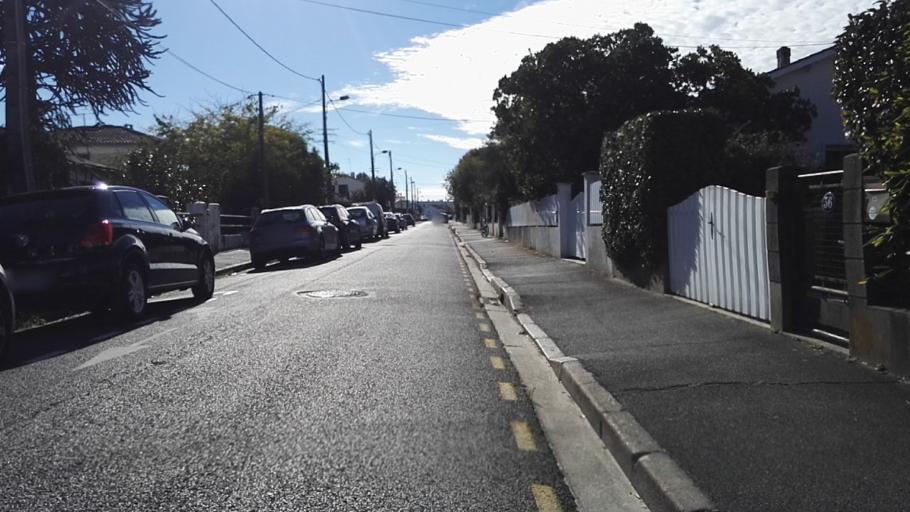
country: FR
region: Aquitaine
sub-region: Departement de la Gironde
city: Eysines
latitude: 44.8595
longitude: -0.6347
